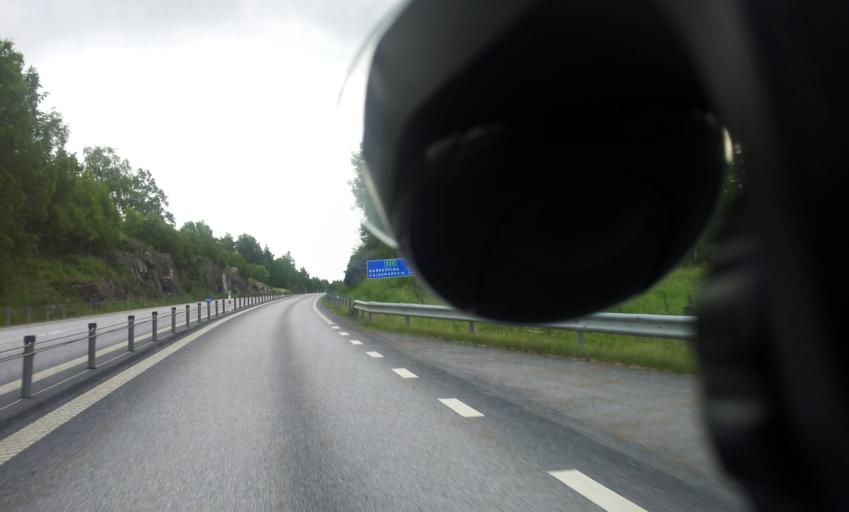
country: SE
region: Kalmar
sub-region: Vasterviks Kommun
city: Forserum
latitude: 57.9618
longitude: 16.4468
